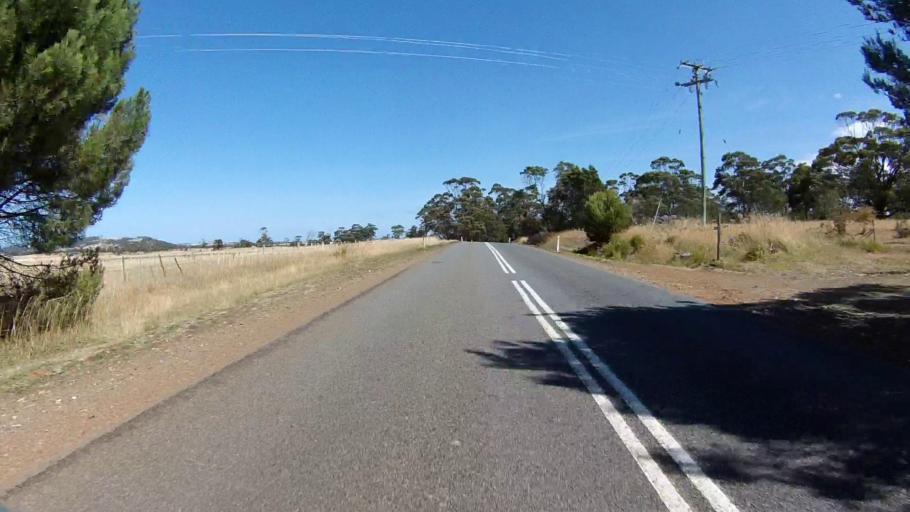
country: AU
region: Tasmania
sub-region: Sorell
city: Sorell
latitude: -42.2873
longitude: 147.9962
